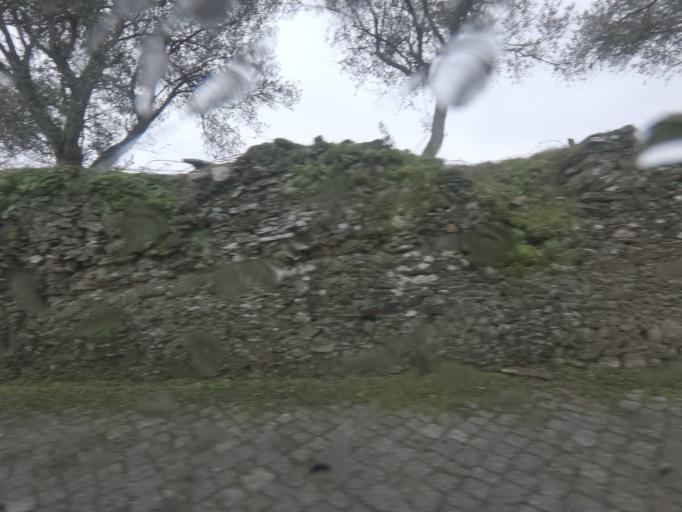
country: PT
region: Vila Real
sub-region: Peso da Regua
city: Peso da Regua
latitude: 41.1830
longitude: -7.7164
